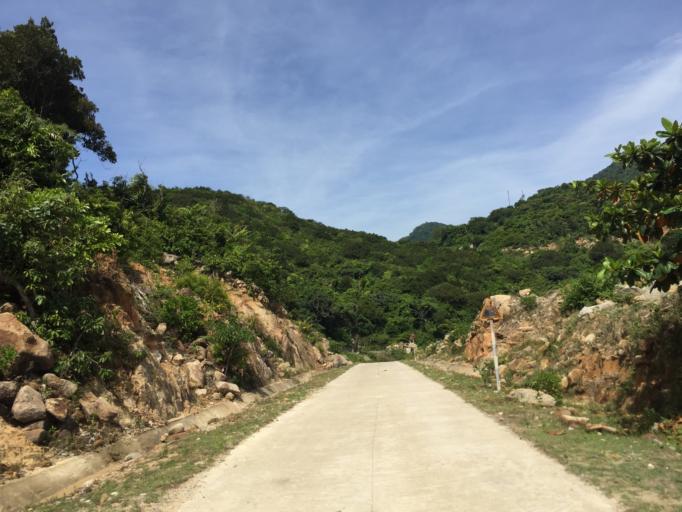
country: VN
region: Quang Nam
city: Hoi An
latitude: 15.9634
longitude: 108.5112
